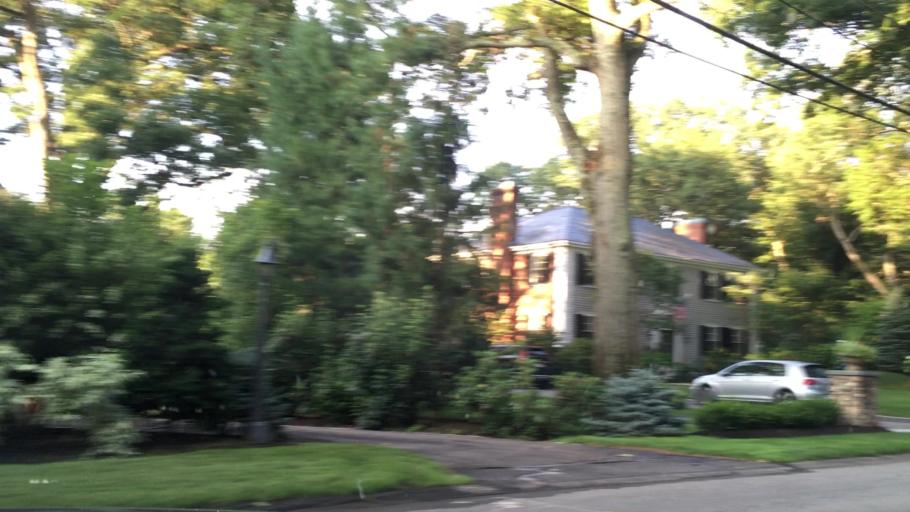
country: US
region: Massachusetts
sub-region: Norfolk County
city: Wellesley
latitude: 42.3158
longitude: -71.2858
